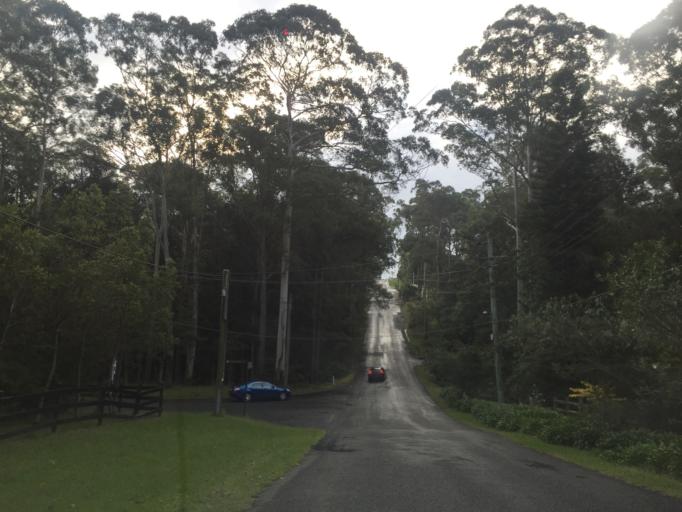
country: AU
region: New South Wales
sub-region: The Hills Shire
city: Glenhaven
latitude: -33.6839
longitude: 151.0215
